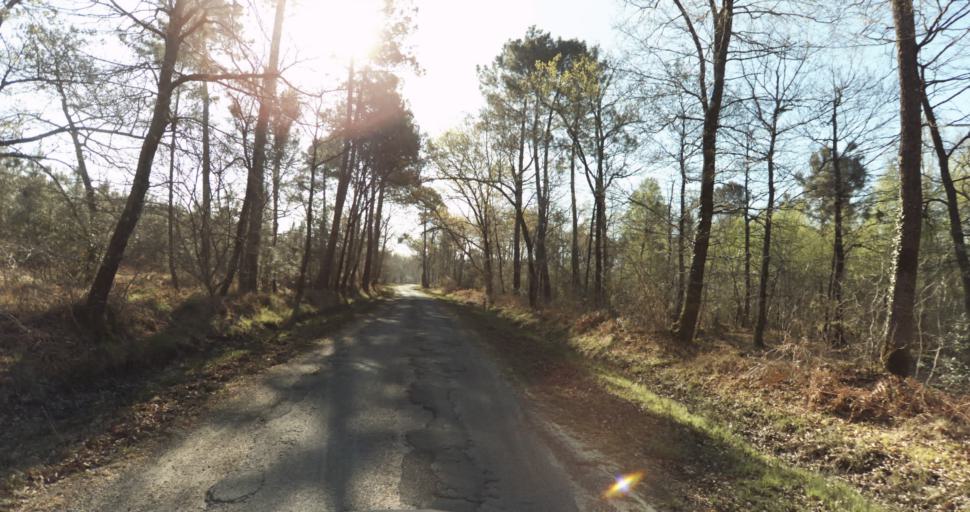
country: FR
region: Aquitaine
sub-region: Departement de la Gironde
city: Martignas-sur-Jalle
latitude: 44.8069
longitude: -0.8475
